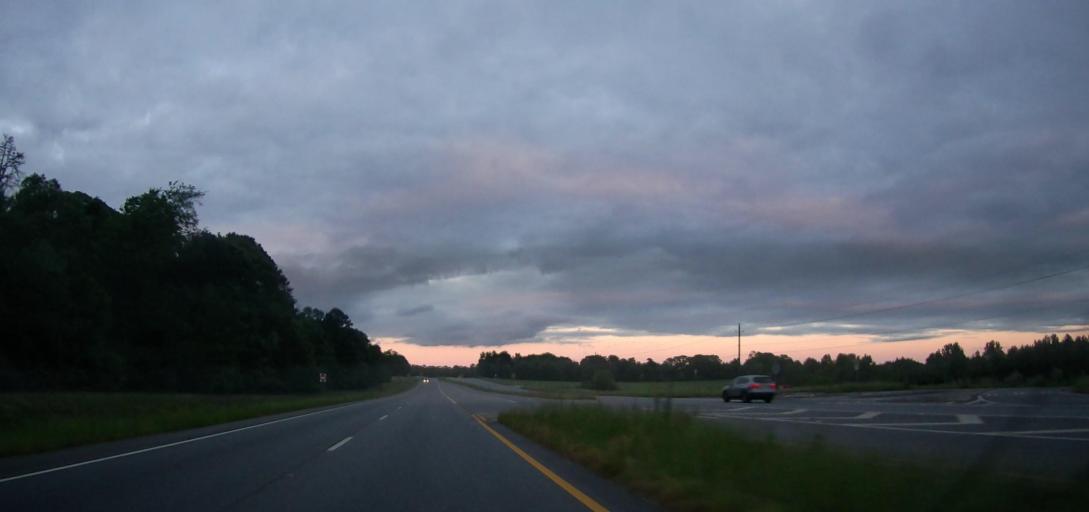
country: US
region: Georgia
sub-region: Jackson County
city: Arcade
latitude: 34.0618
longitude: -83.5206
